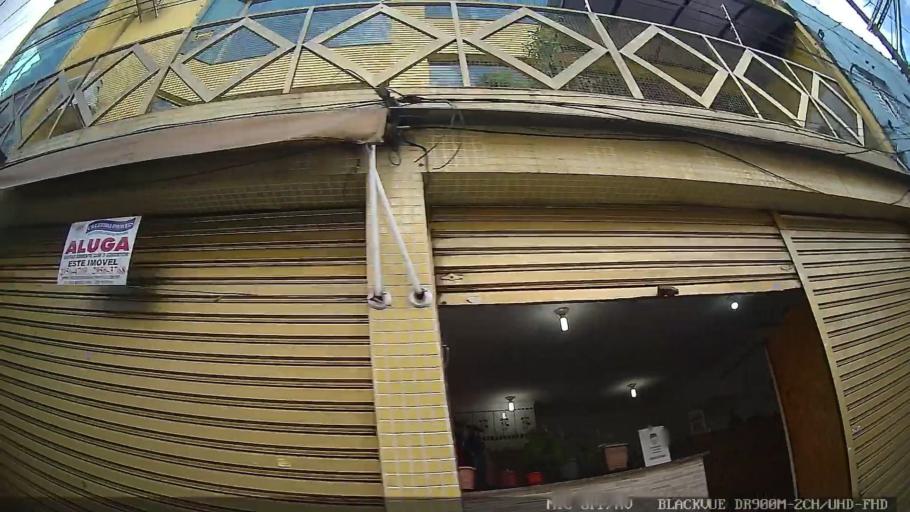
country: BR
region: Sao Paulo
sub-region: Guarulhos
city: Guarulhos
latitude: -23.4976
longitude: -46.4589
